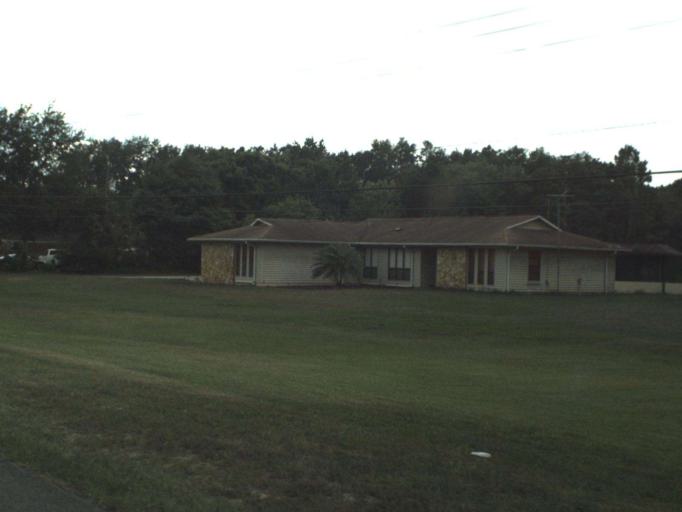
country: US
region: Florida
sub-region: Brevard County
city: Titusville
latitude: 28.5813
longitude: -80.8471
